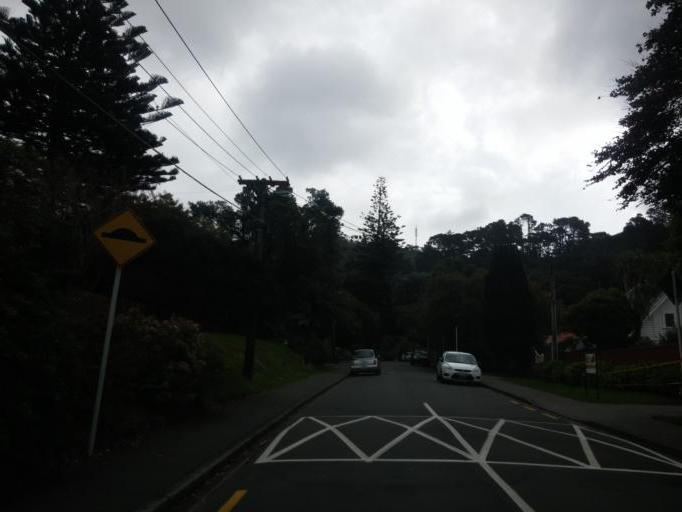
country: NZ
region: Wellington
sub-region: Wellington City
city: Wellington
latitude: -41.2432
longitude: 174.7911
